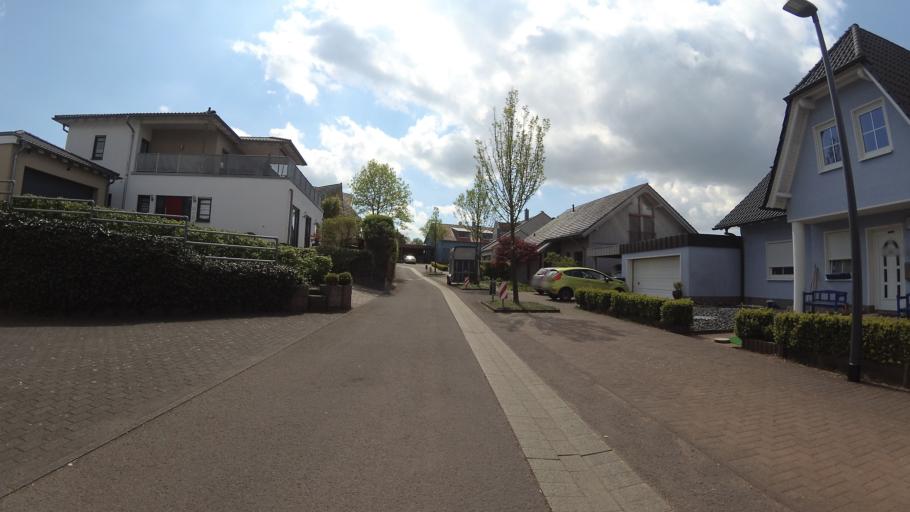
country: DE
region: Saarland
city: Wadern
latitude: 49.5338
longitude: 6.8874
